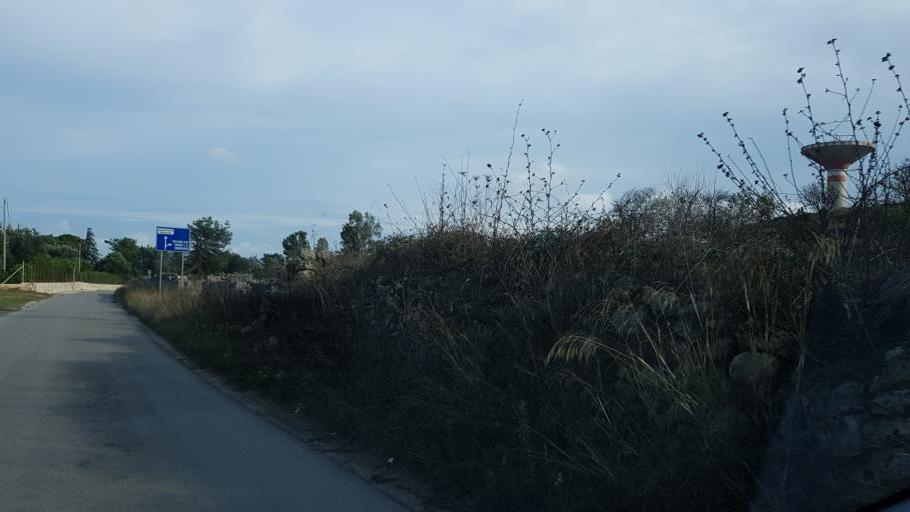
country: IT
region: Apulia
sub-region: Provincia di Brindisi
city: Oria
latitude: 40.5001
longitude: 17.6531
